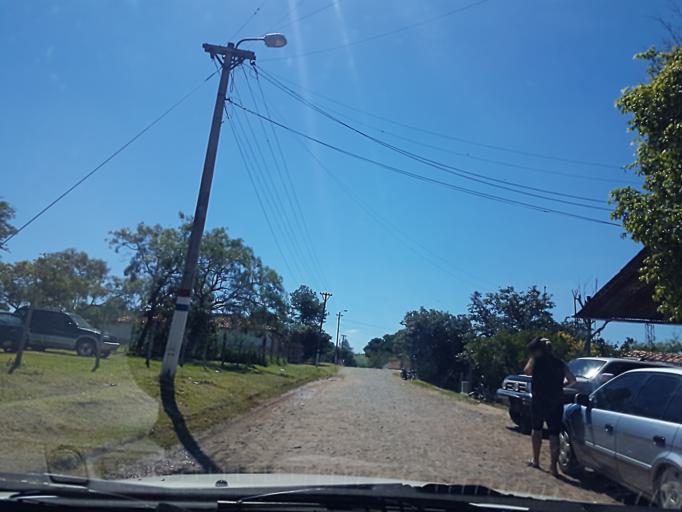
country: PY
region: Cordillera
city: Atyra
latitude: -25.2843
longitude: -57.1751
